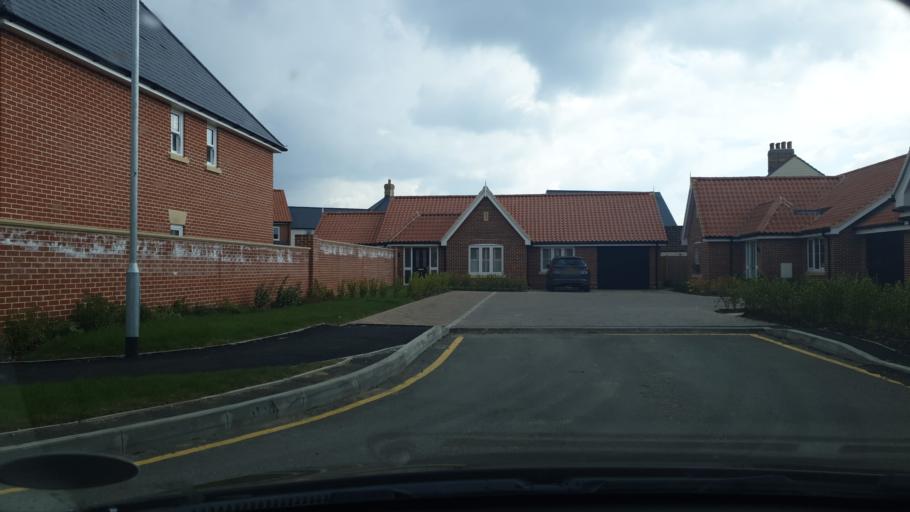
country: GB
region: England
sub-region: Essex
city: Manningtree
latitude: 51.9411
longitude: 1.0499
